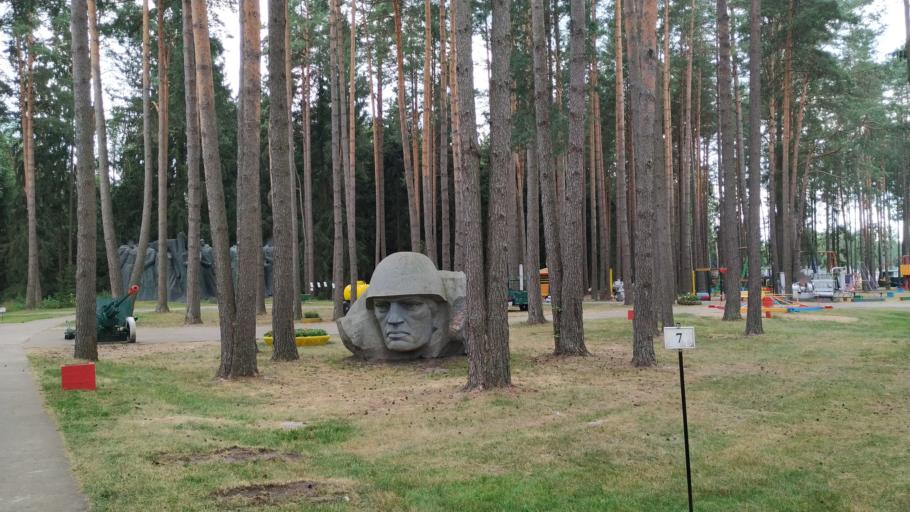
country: LT
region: Alytaus apskritis
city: Druskininkai
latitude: 54.0223
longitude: 24.0794
